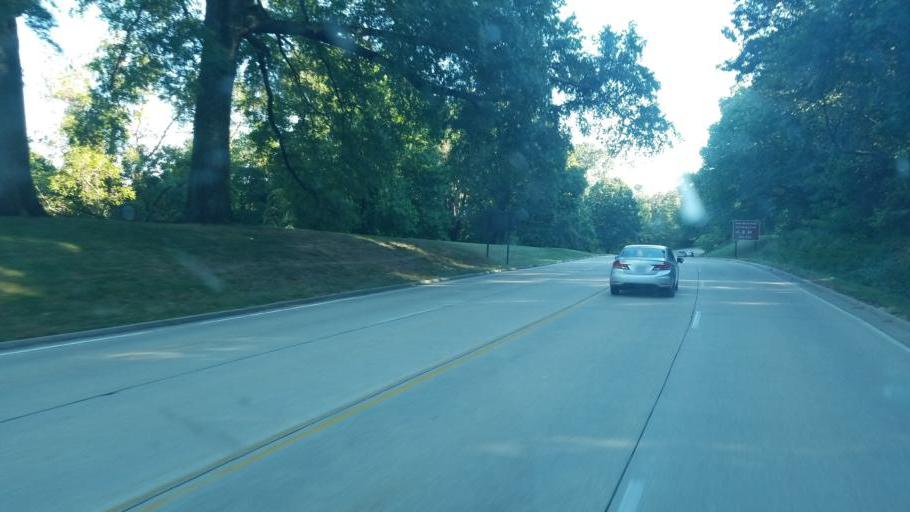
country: US
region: Virginia
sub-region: Fairfax County
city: Fort Hunt
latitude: 38.7215
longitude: -77.0440
